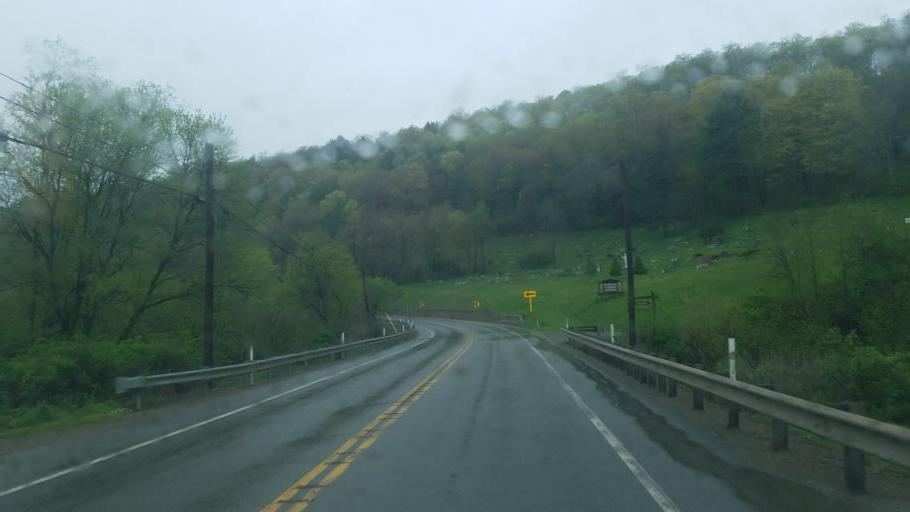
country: US
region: Pennsylvania
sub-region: Potter County
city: Coudersport
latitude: 41.7581
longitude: -78.0524
